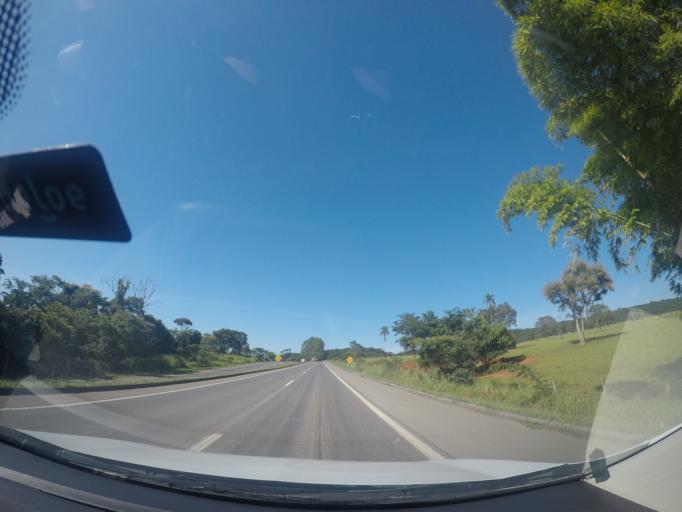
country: BR
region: Goias
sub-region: Pontalina
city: Pontalina
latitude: -17.4374
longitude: -49.2310
